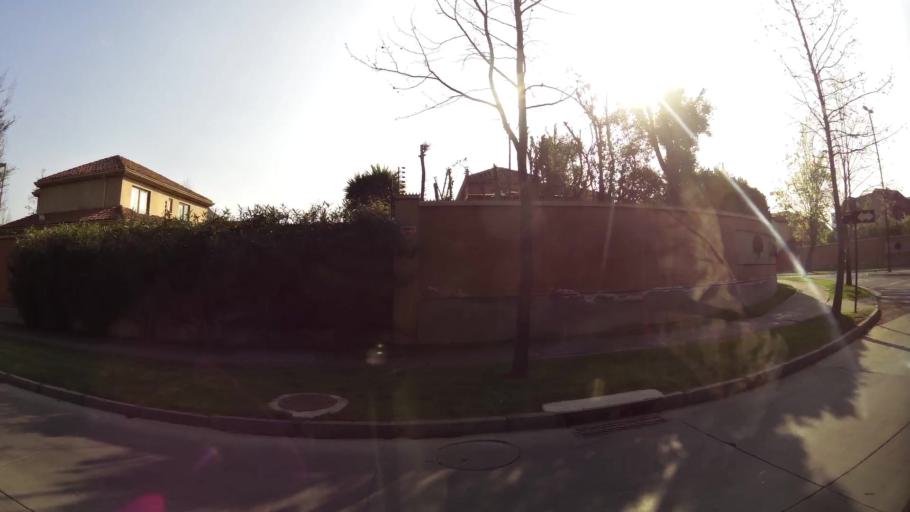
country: CL
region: Santiago Metropolitan
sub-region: Provincia de Santiago
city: Villa Presidente Frei, Nunoa, Santiago, Chile
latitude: -33.3577
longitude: -70.5342
